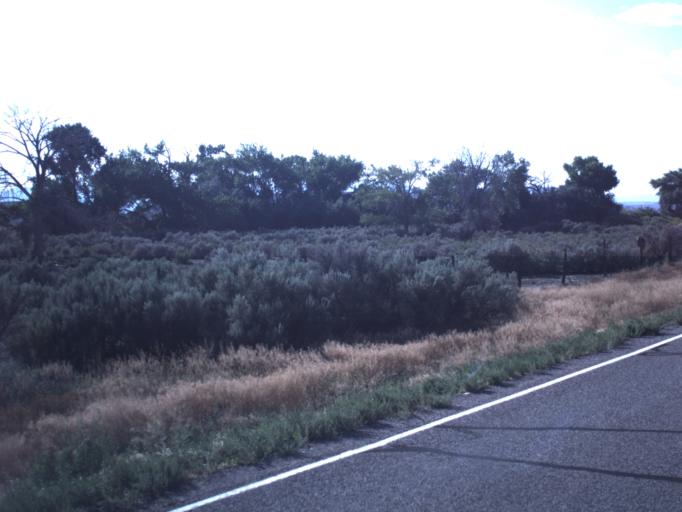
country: US
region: Utah
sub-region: Emery County
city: Huntington
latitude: 39.4154
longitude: -110.8561
